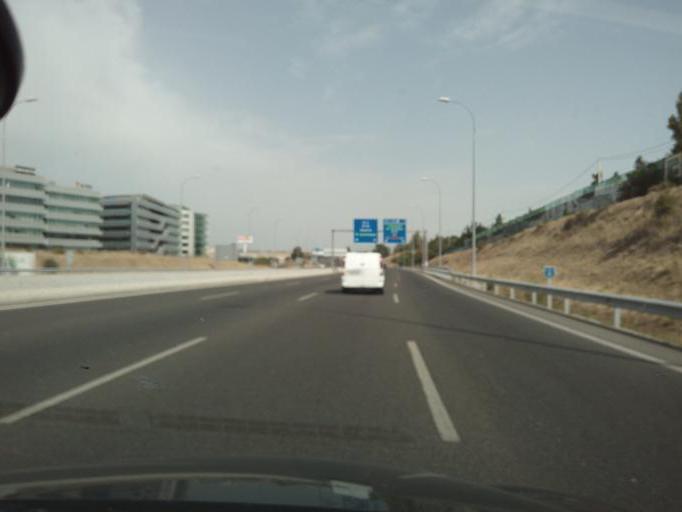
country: ES
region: Madrid
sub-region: Provincia de Madrid
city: Hortaleza
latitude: 40.4756
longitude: -3.6307
